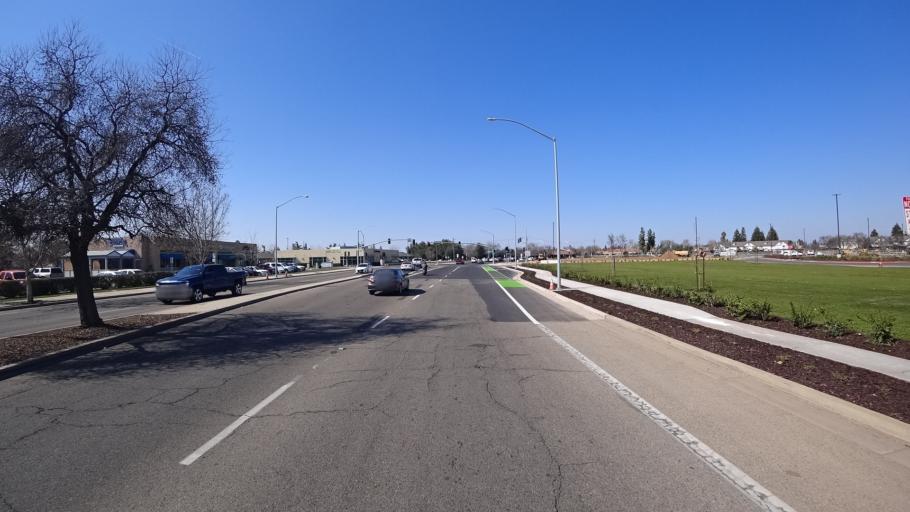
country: US
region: California
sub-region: Fresno County
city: Clovis
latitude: 36.8397
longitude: -119.7552
